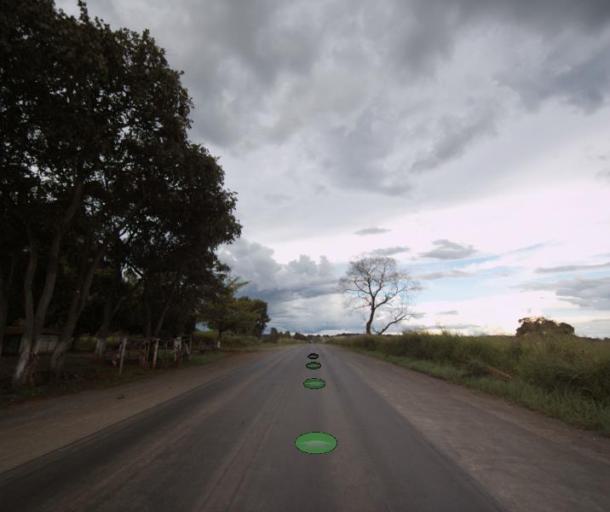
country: BR
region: Goias
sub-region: Itapaci
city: Itapaci
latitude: -15.0591
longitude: -49.4502
